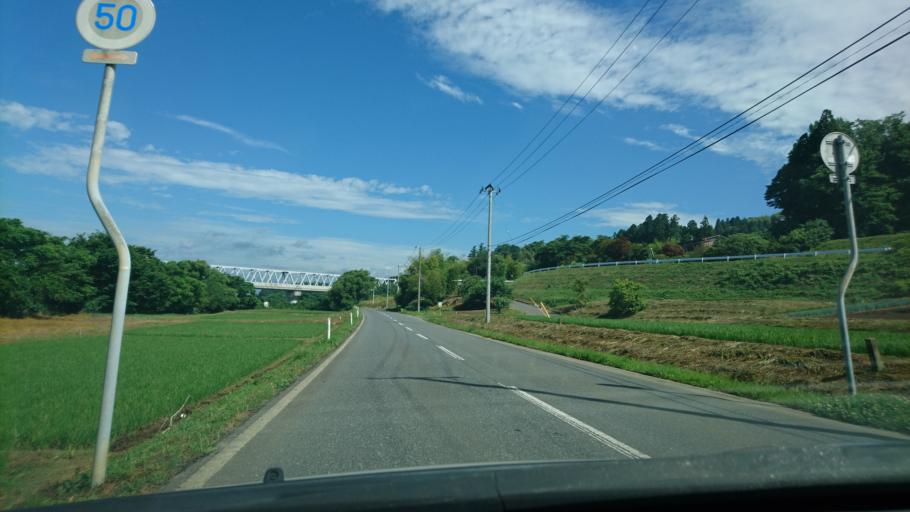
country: JP
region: Iwate
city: Ichinoseki
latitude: 38.9732
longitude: 141.1601
